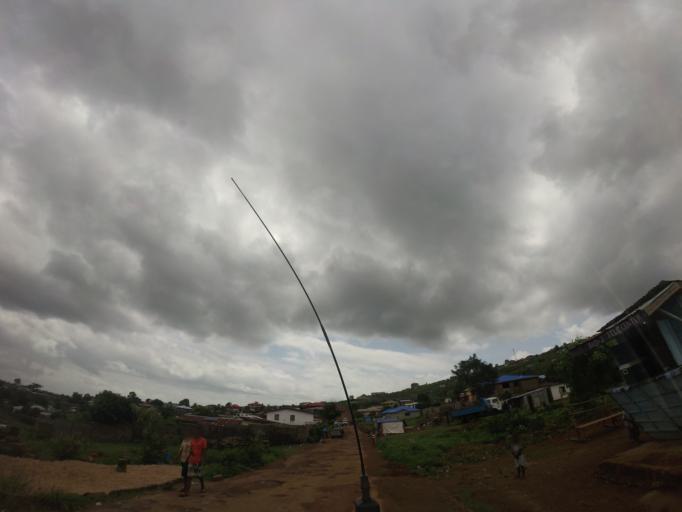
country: SL
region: Western Area
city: Hastings
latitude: 8.3830
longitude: -13.1282
